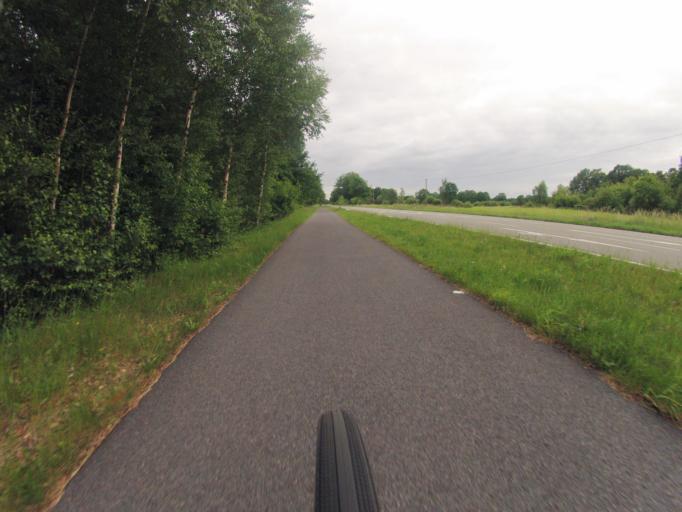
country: DE
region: North Rhine-Westphalia
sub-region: Regierungsbezirk Munster
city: Birgte
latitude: 52.2144
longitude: 7.6756
